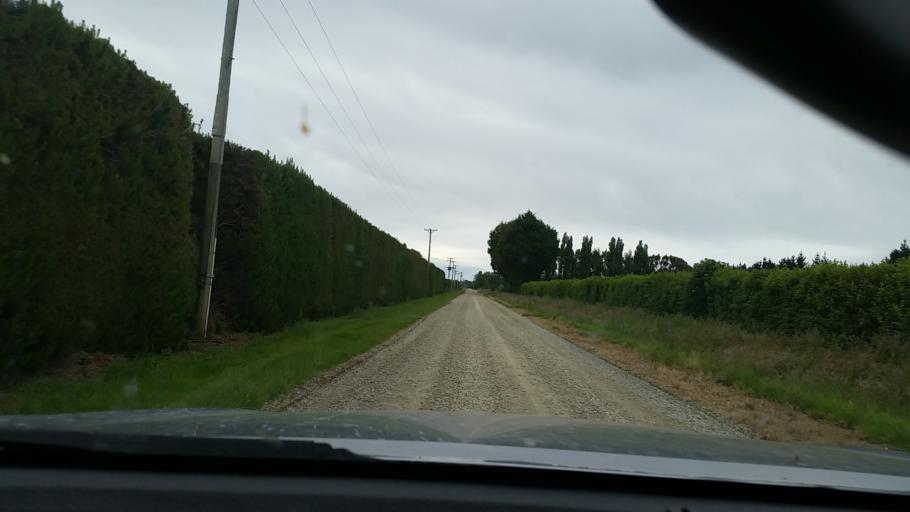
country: NZ
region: Southland
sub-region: Invercargill City
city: Invercargill
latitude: -46.2802
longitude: 168.3674
